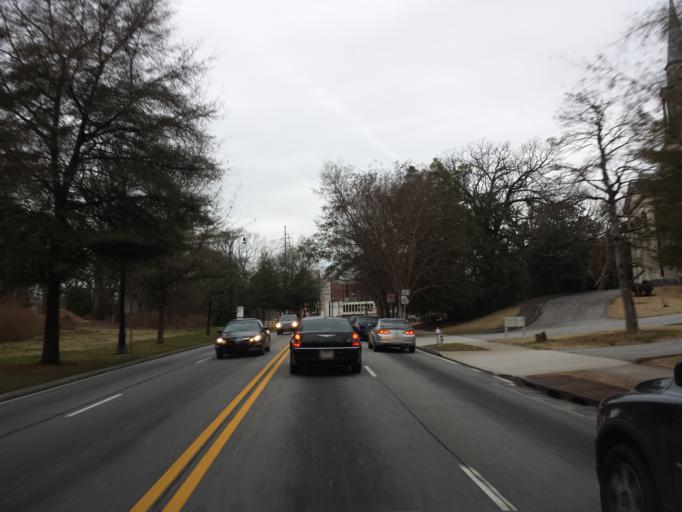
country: US
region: Georgia
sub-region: DeKalb County
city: Druid Hills
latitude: 33.7742
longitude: -84.3473
